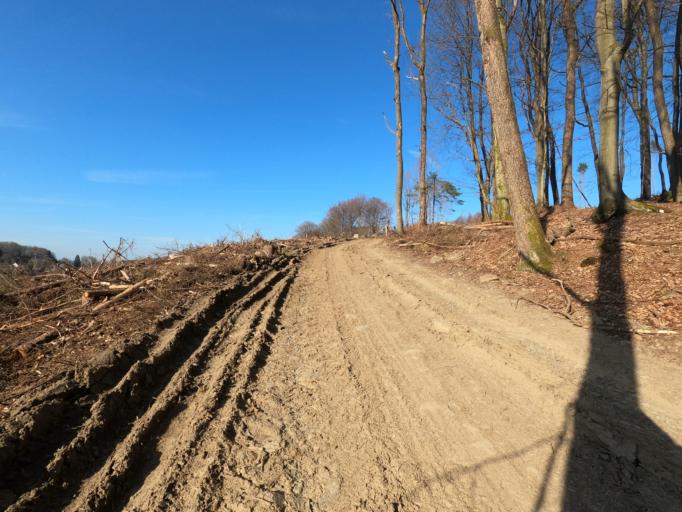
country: DE
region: North Rhine-Westphalia
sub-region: Regierungsbezirk Arnsberg
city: Herscheid
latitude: 51.1733
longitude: 7.7172
